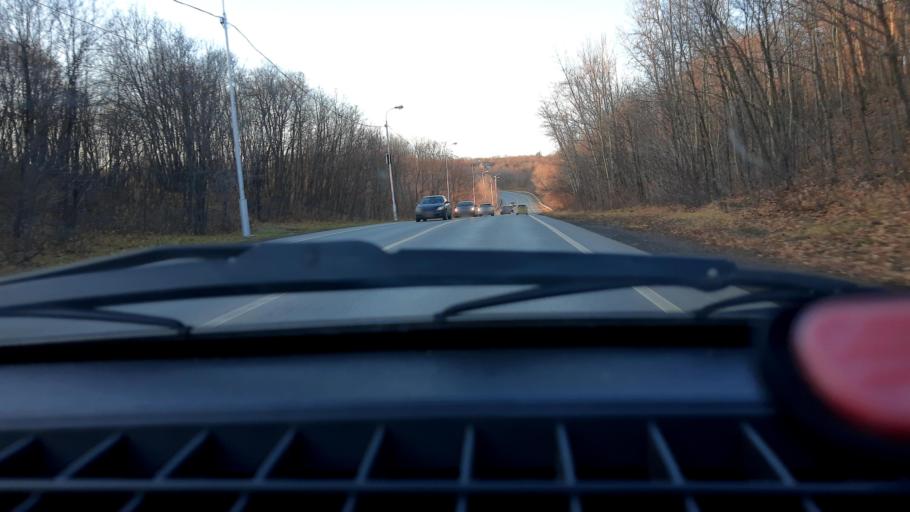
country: RU
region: Bashkortostan
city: Ufa
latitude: 54.8799
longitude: 56.0610
